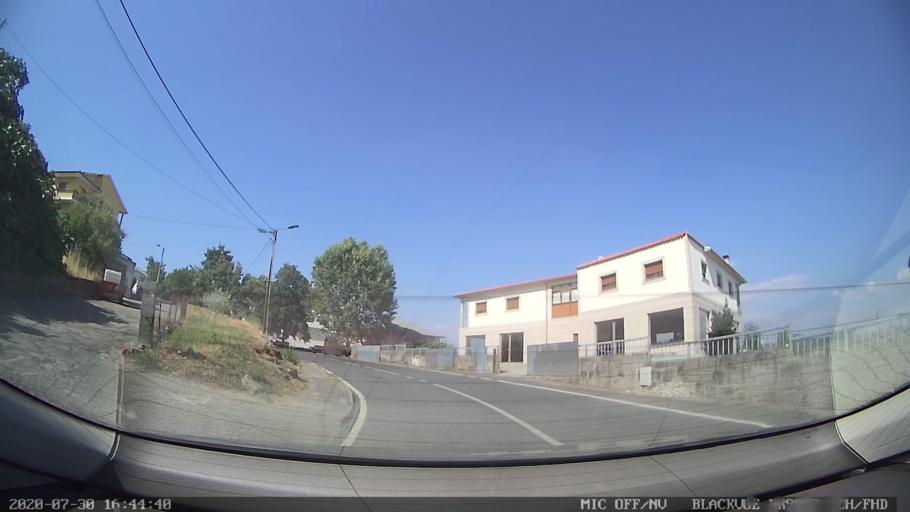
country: PT
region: Vila Real
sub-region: Sabrosa
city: Sabrosa
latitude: 41.2814
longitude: -7.4759
